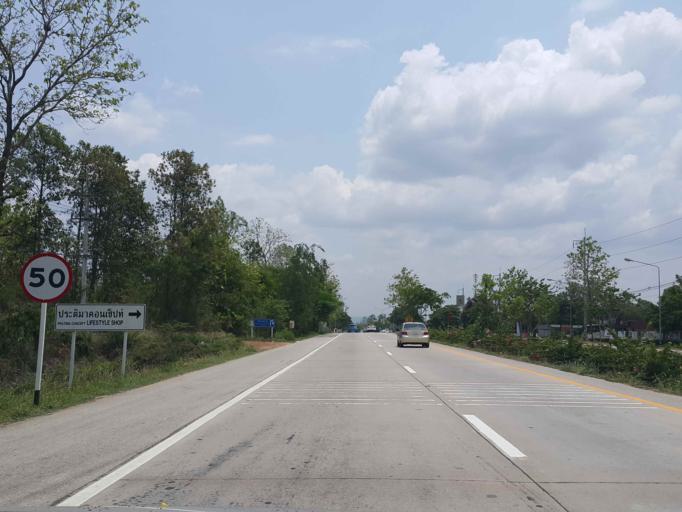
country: TH
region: Lampang
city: Hang Chat
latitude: 18.2981
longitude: 99.4121
